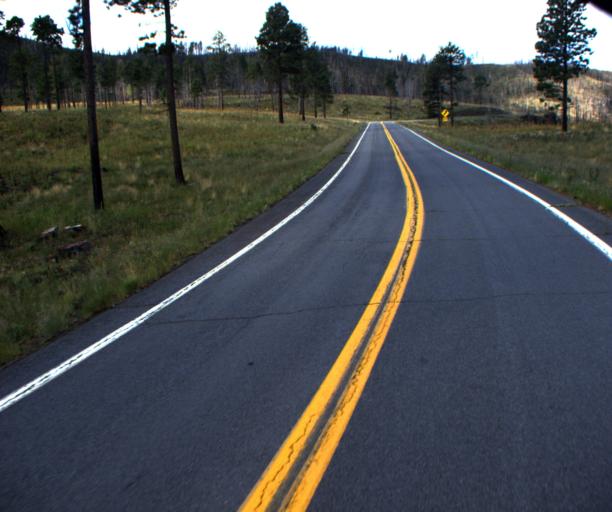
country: US
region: Arizona
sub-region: Apache County
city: Eagar
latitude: 34.0501
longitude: -109.3570
